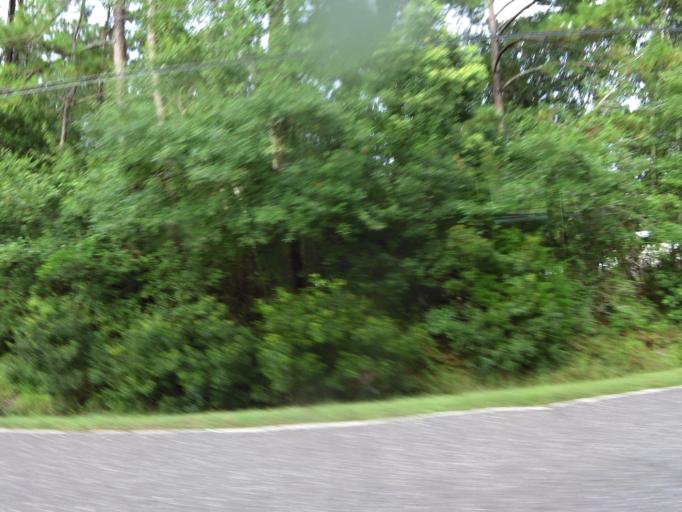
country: US
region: Florida
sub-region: Nassau County
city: Nassau Village-Ratliff
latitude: 30.4183
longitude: -81.7612
